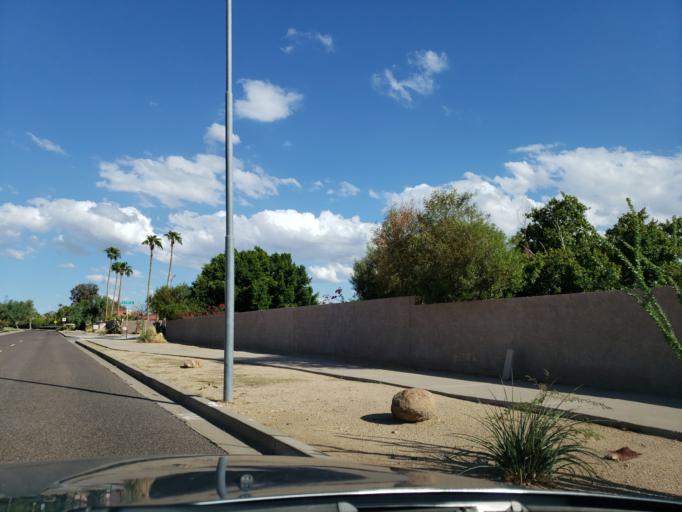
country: US
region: Arizona
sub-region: Maricopa County
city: Scottsdale
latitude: 33.5860
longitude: -111.8444
